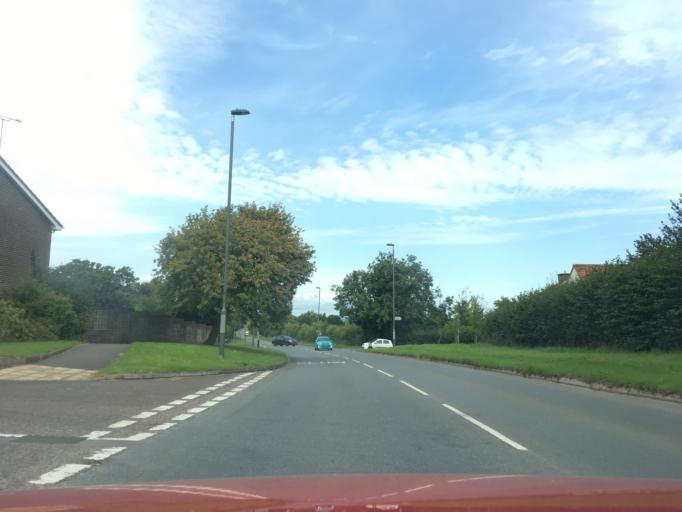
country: GB
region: England
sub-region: South Gloucestershire
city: Thornbury
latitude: 51.6094
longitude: -2.5050
